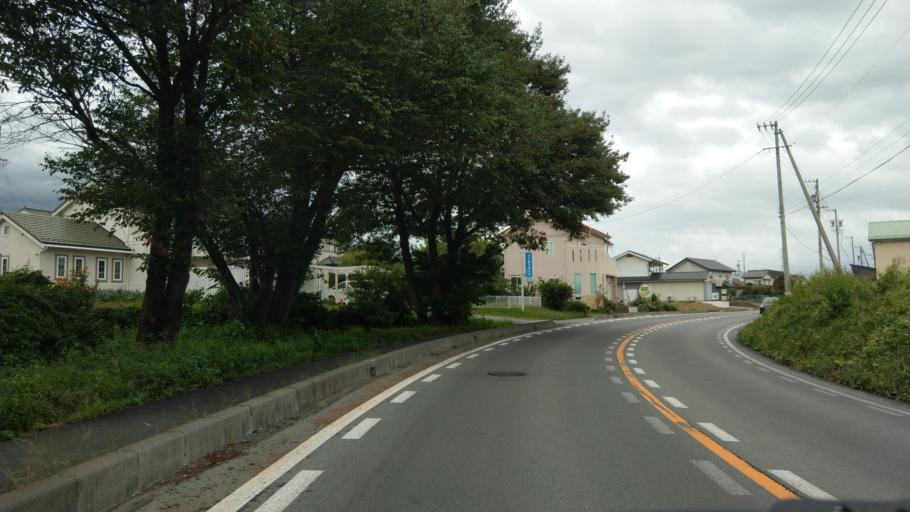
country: JP
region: Nagano
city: Komoro
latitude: 36.2972
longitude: 138.4597
